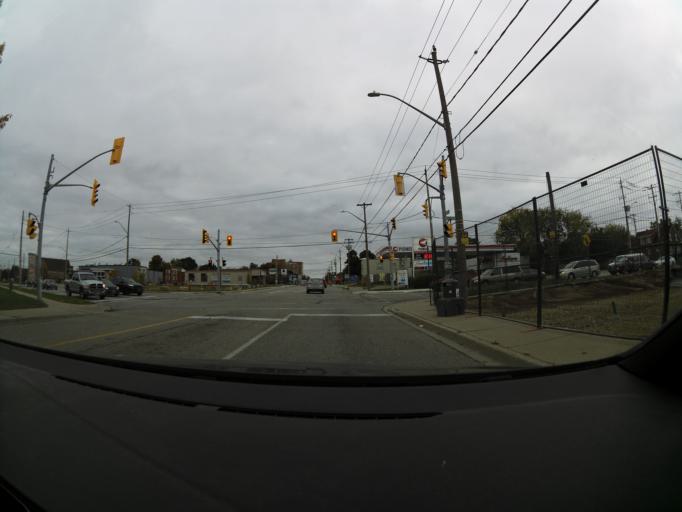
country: CA
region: Ontario
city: Kitchener
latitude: 43.4419
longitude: -80.4719
